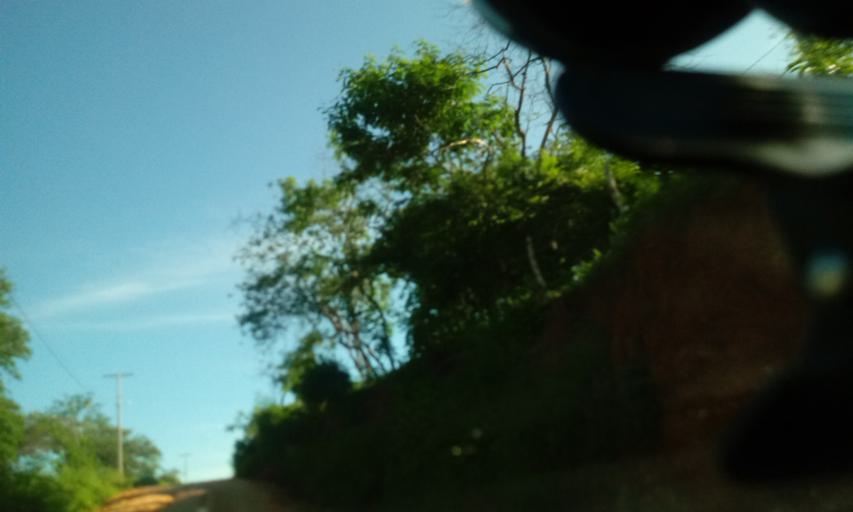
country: BR
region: Bahia
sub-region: Riacho De Santana
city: Riacho de Santana
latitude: -13.8347
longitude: -42.7686
